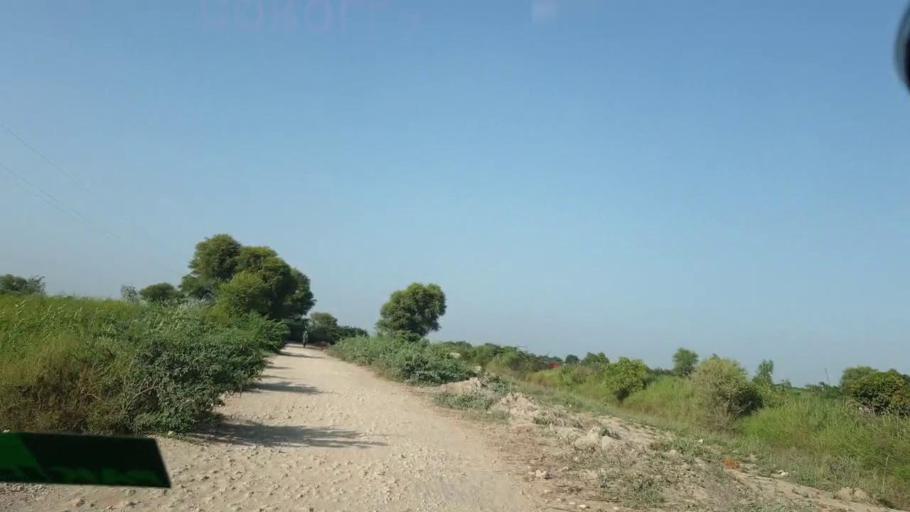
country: PK
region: Sindh
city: Naukot
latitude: 24.7399
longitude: 69.2202
